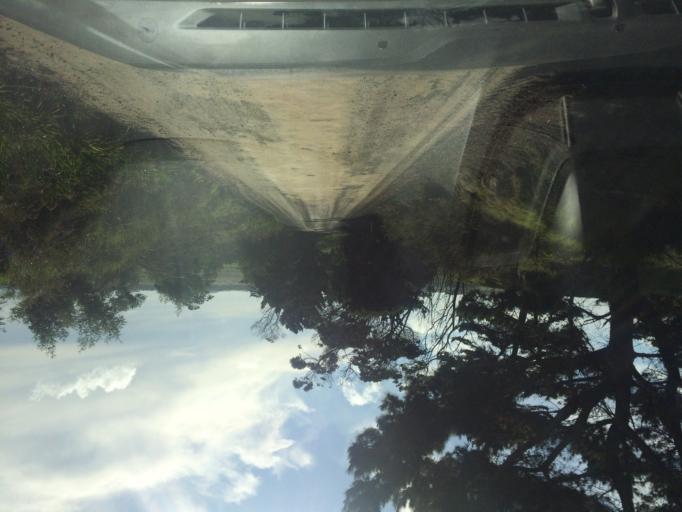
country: NZ
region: Northland
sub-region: Kaipara District
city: Dargaville
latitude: -36.0275
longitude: 173.8803
